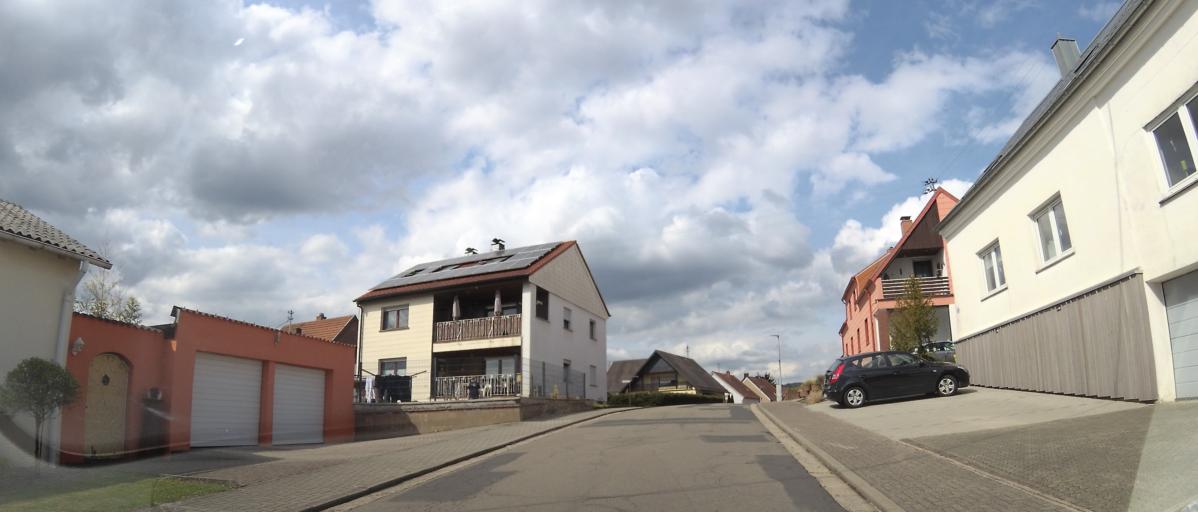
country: DE
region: Saarland
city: Bexbach
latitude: 49.3573
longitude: 7.2617
